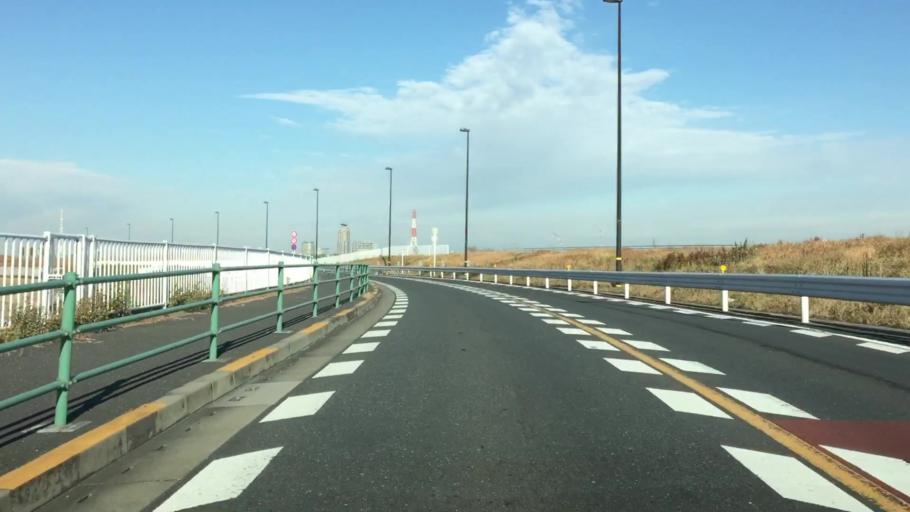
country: JP
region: Saitama
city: Kawaguchi
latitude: 35.7671
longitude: 139.7564
